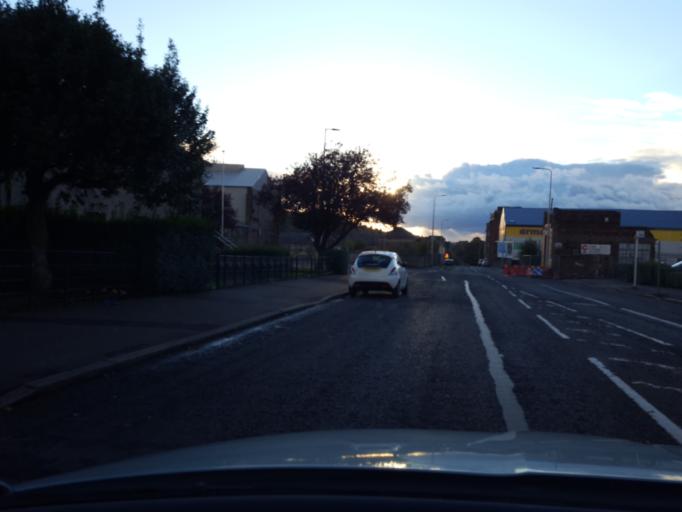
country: GB
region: Scotland
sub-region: Dundee City
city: Dundee
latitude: 56.4716
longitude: -2.9962
